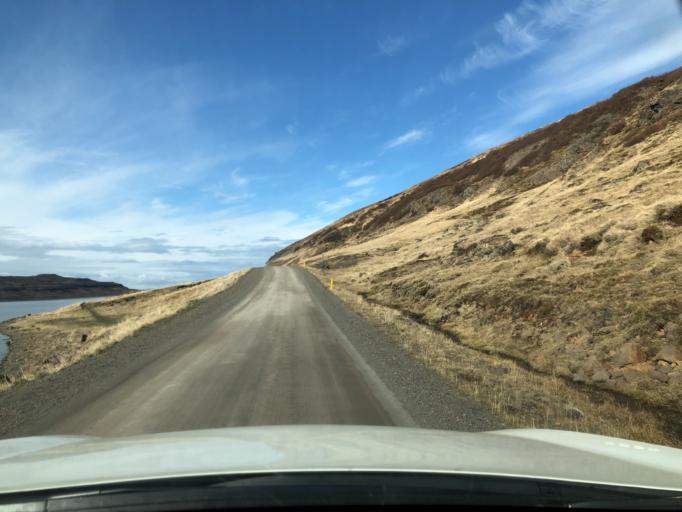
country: IS
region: West
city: Borgarnes
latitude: 65.0596
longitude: -21.5914
